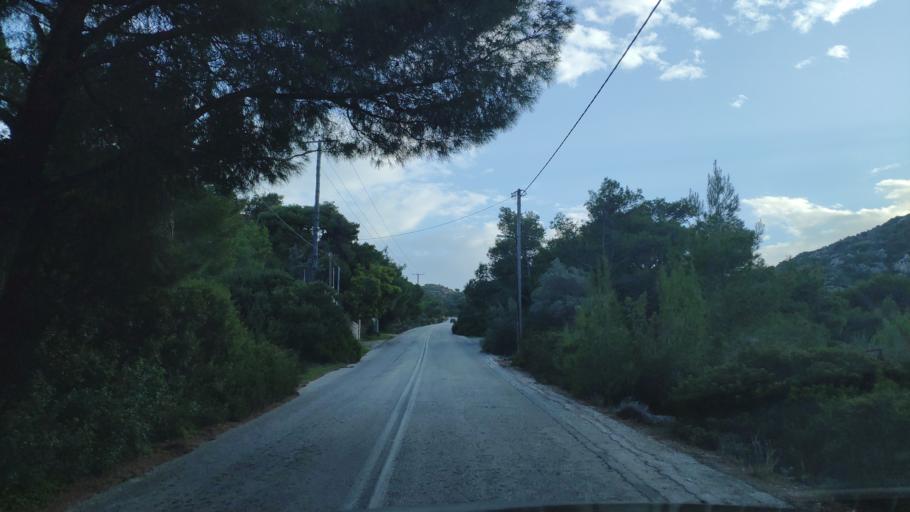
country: GR
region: Attica
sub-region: Nomarchia Anatolikis Attikis
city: Limin Mesoyaias
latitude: 37.9146
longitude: 24.0143
